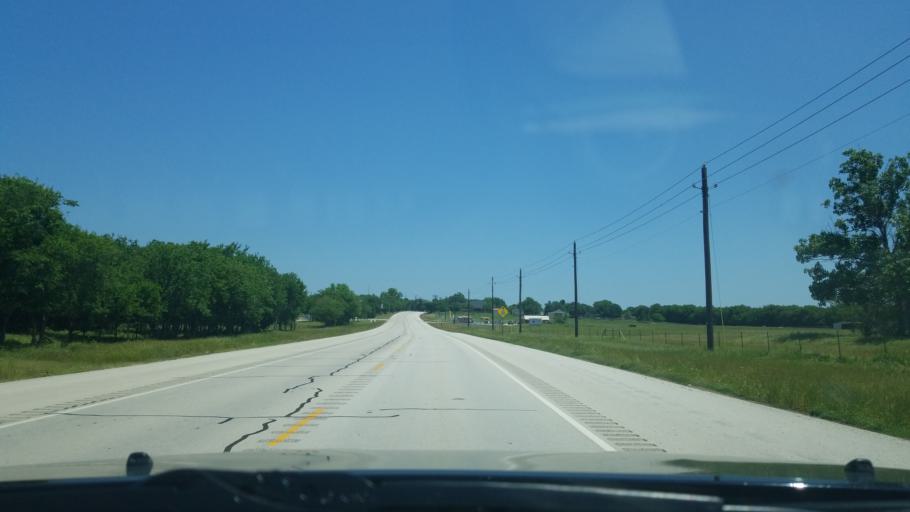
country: US
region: Texas
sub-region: Denton County
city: Krum
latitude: 33.2526
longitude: -97.2416
